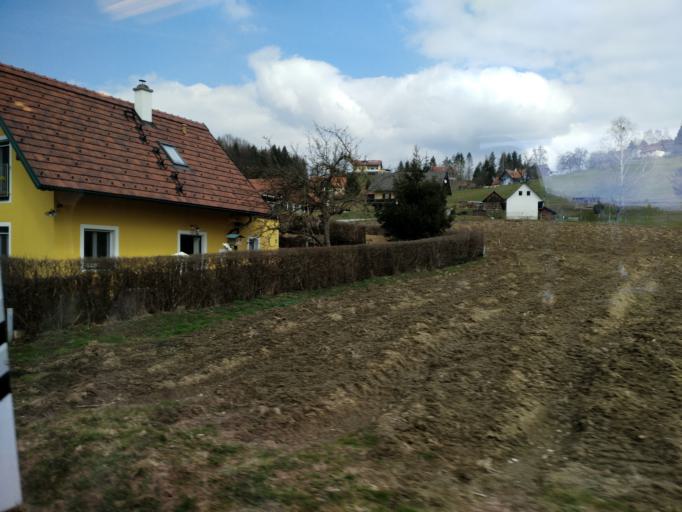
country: AT
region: Styria
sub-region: Politischer Bezirk Deutschlandsberg
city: Hollenegg
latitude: 46.7958
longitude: 15.2336
